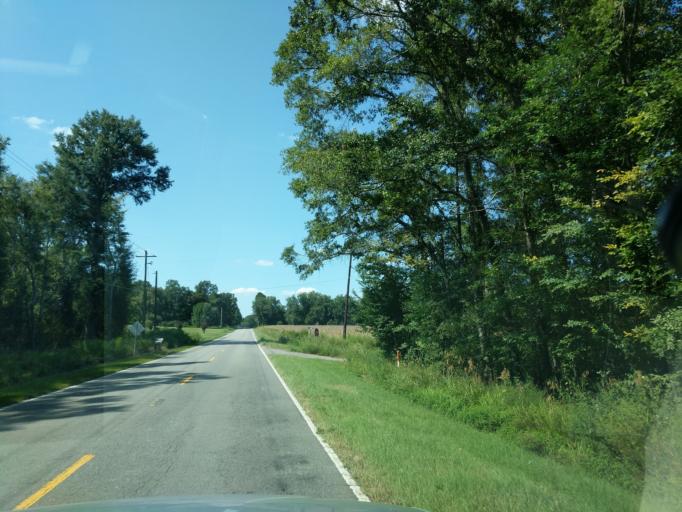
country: US
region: South Carolina
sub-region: Lexington County
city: Leesville
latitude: 34.0112
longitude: -81.5173
